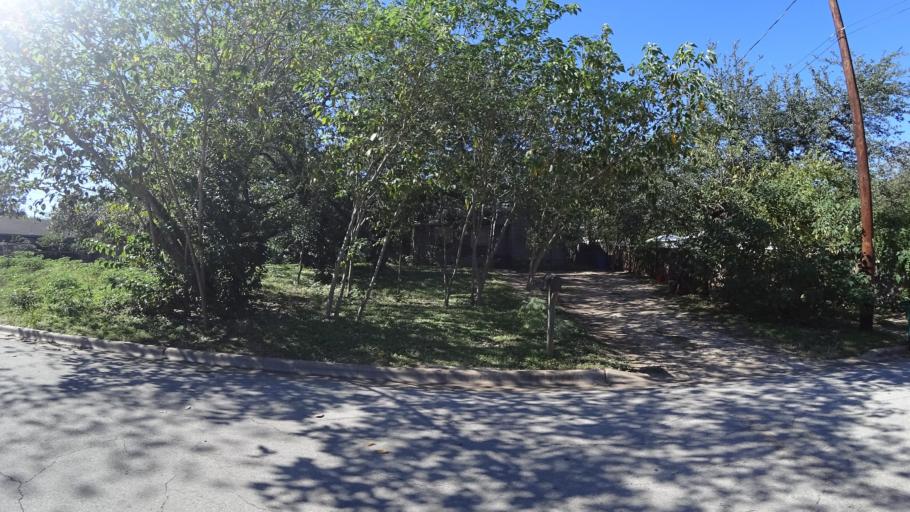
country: US
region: Texas
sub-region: Travis County
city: Rollingwood
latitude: 30.2251
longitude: -97.7795
